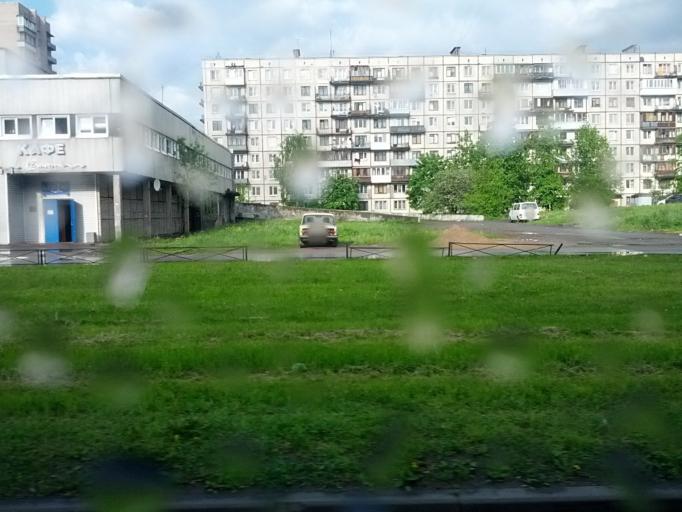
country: RU
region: St.-Petersburg
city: Obukhovo
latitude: 59.8960
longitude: 30.4759
